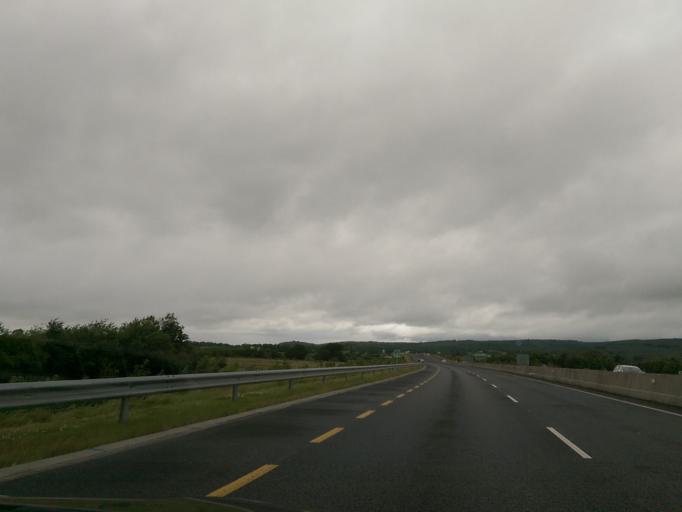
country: IE
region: Munster
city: Moyross
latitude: 52.6778
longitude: -8.7069
